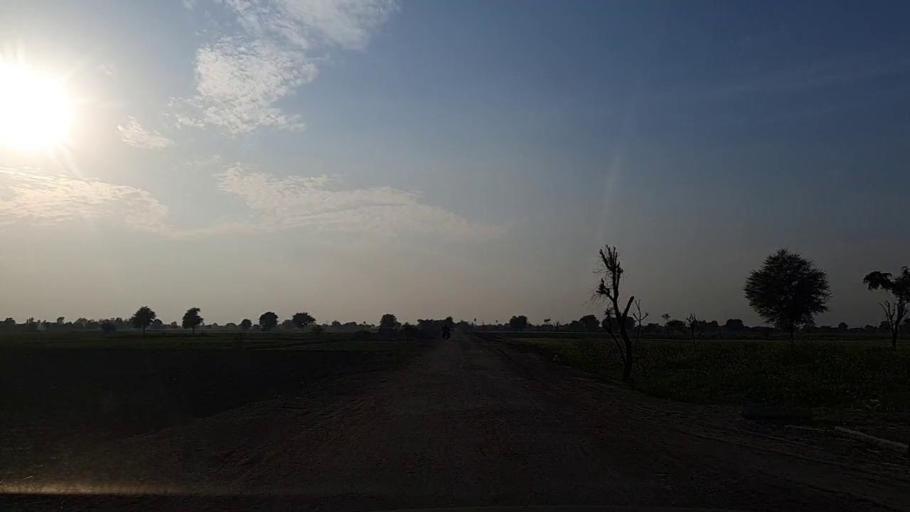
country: PK
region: Sindh
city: Jam Sahib
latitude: 26.3952
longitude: 68.5406
